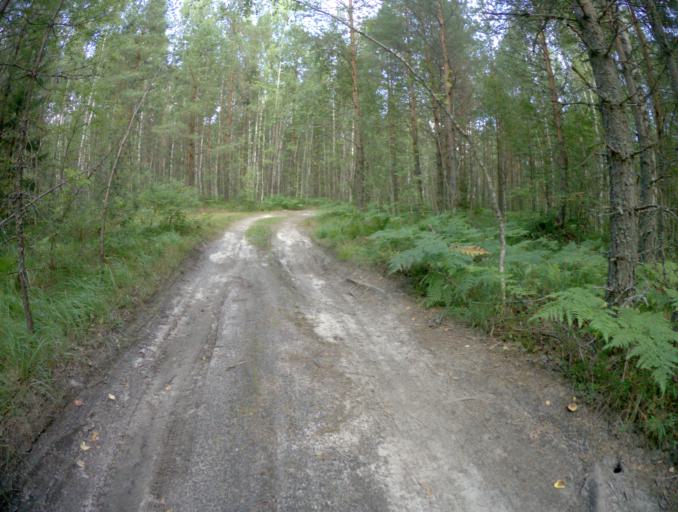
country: RU
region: Vladimir
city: Raduzhnyy
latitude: 55.9522
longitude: 40.1973
